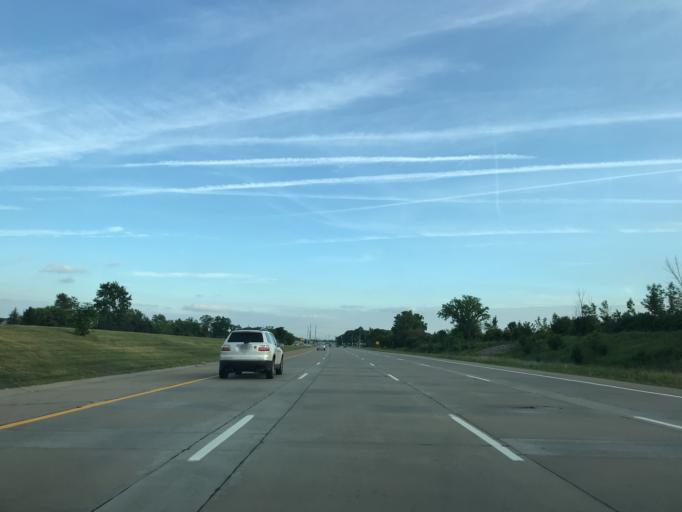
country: US
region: Michigan
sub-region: Oakland County
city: Walled Lake
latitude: 42.5159
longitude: -83.4467
